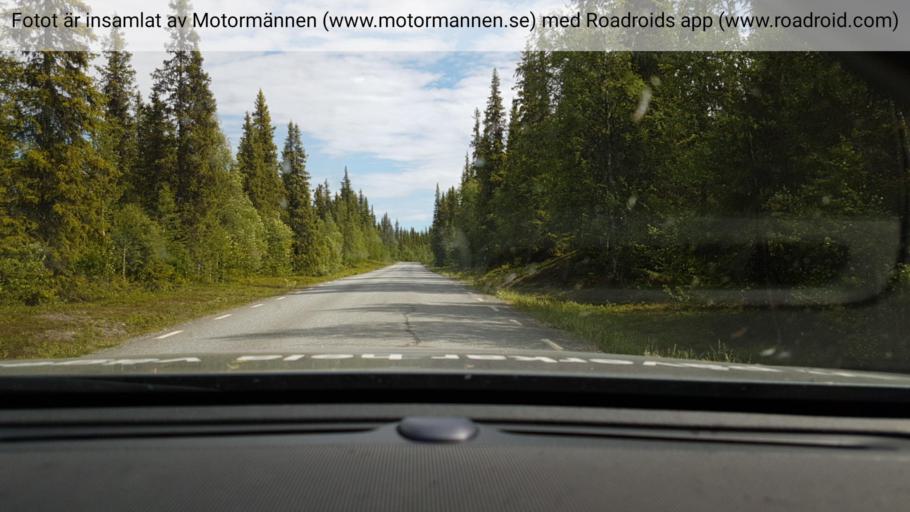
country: SE
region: Vaesterbotten
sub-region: Vilhelmina Kommun
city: Sjoberg
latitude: 65.2267
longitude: 16.0146
